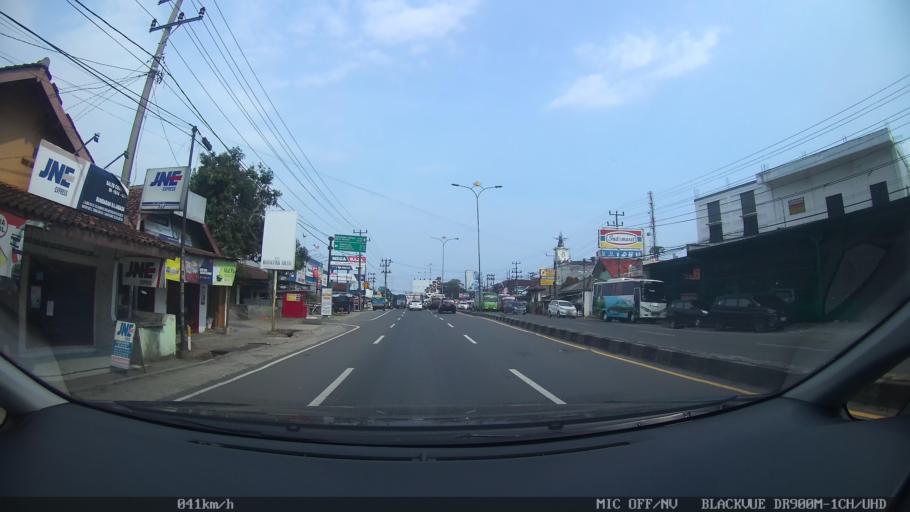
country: ID
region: Lampung
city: Kedaton
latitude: -5.3603
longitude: 105.2243
